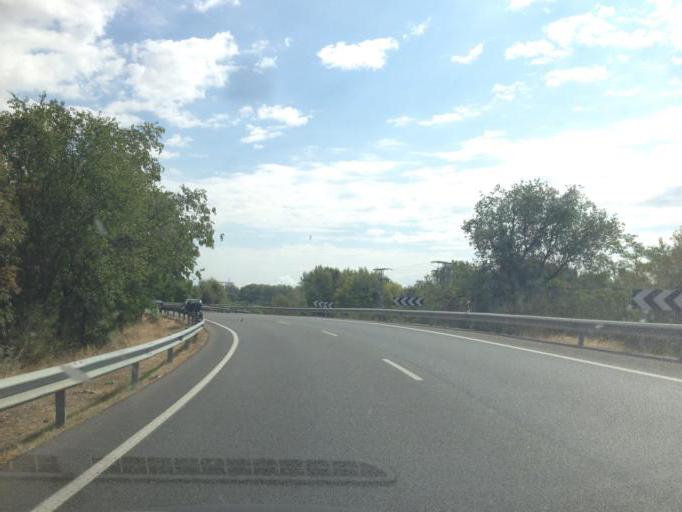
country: ES
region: Madrid
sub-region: Provincia de Madrid
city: San Sebastian de los Reyes
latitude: 40.5827
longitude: -3.5712
